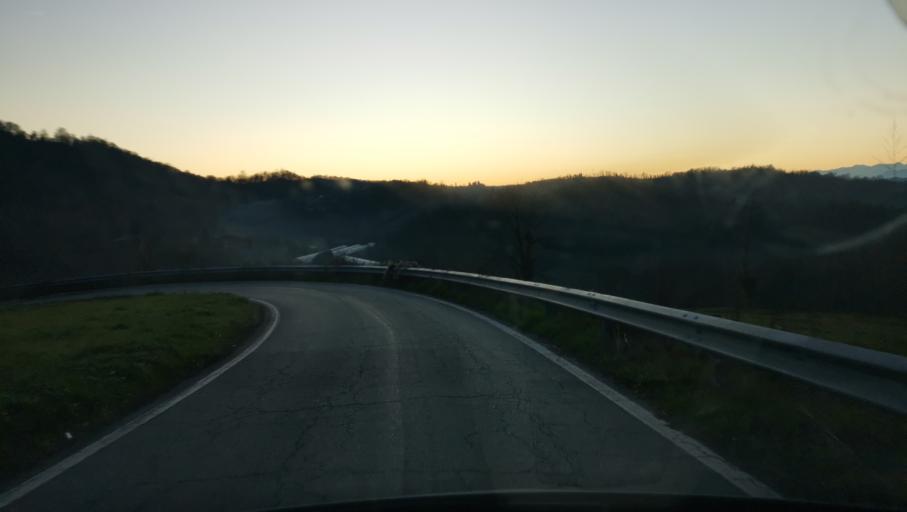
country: IT
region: Piedmont
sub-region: Provincia di Torino
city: Cinzano
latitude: 45.1077
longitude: 7.9180
